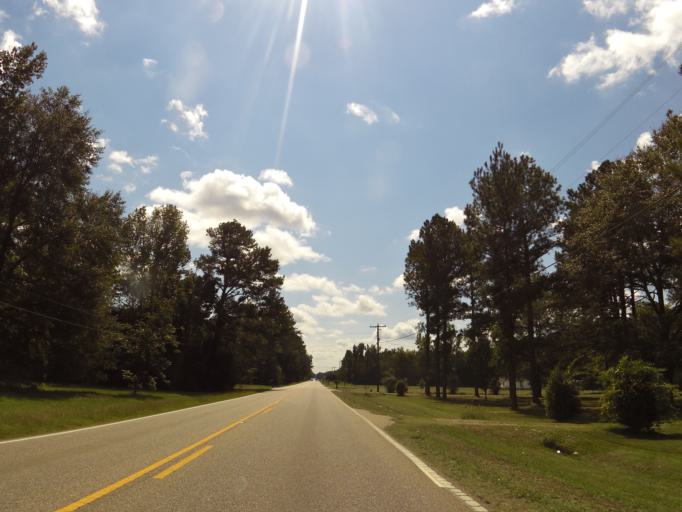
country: US
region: Alabama
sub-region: Dallas County
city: Selma
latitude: 32.4333
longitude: -87.0835
